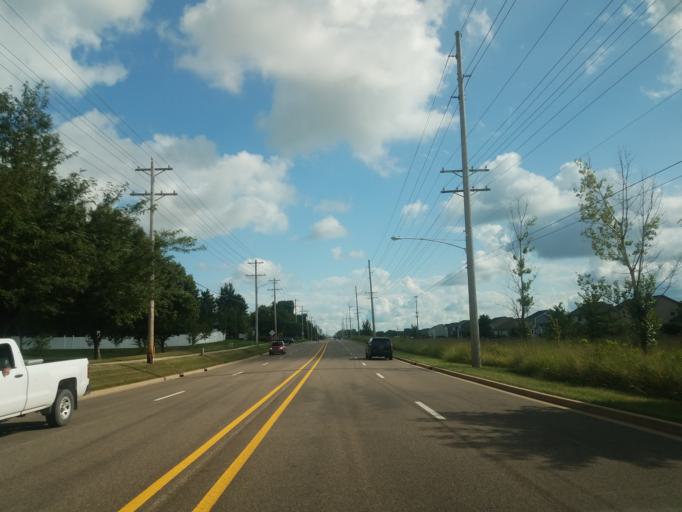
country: US
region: Illinois
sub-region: McLean County
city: Normal
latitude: 40.5081
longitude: -88.9243
